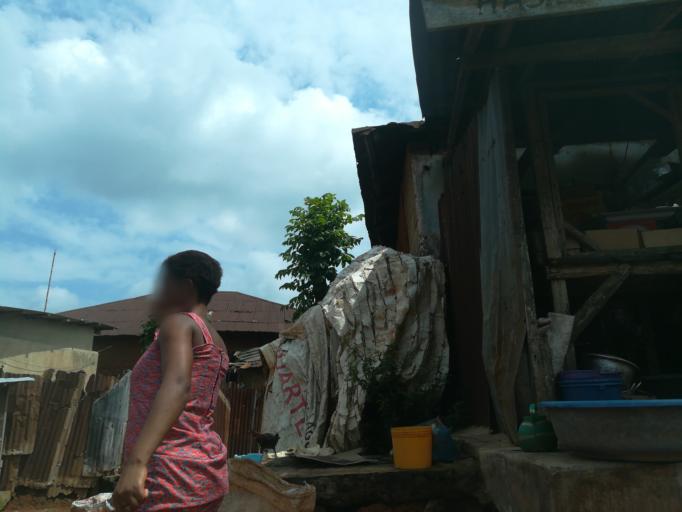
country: NG
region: Lagos
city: Ejirin
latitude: 6.6438
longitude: 3.7132
